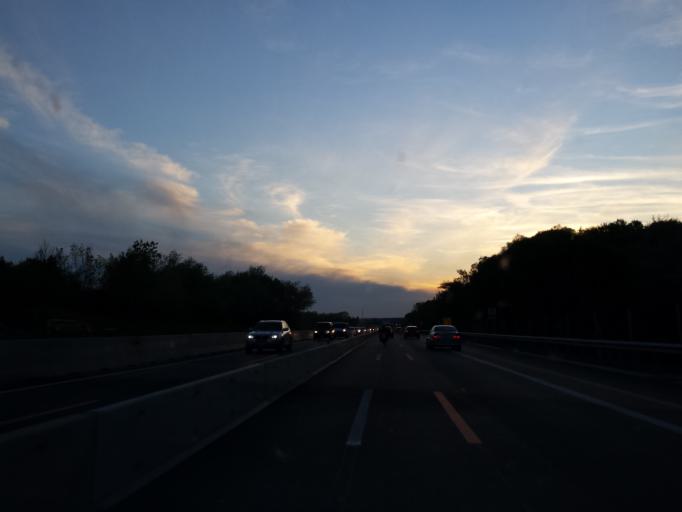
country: AT
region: Lower Austria
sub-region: Politischer Bezirk Wien-Umgebung
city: Fischamend Dorf
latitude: 48.1285
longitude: 16.5721
